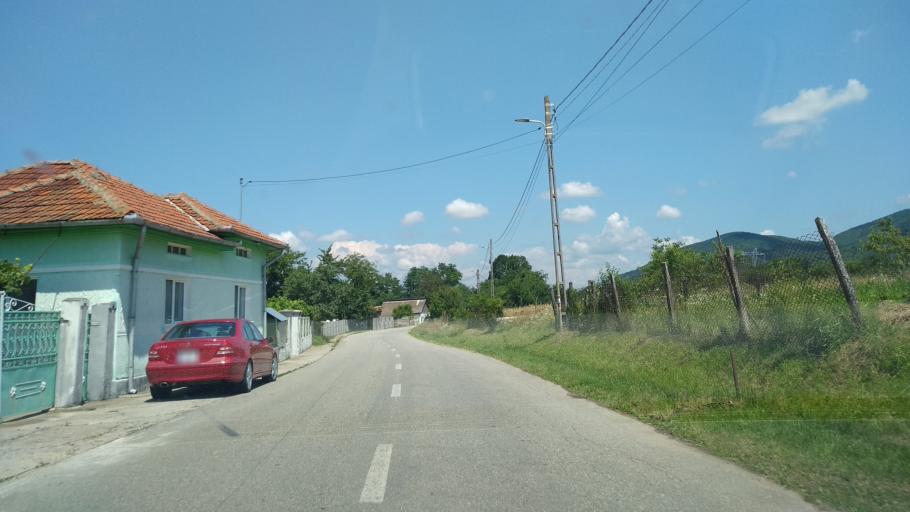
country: RO
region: Hunedoara
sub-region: Comuna Santamaria-Orlea
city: Santamaria-Orlea
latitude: 45.5964
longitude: 23.0091
